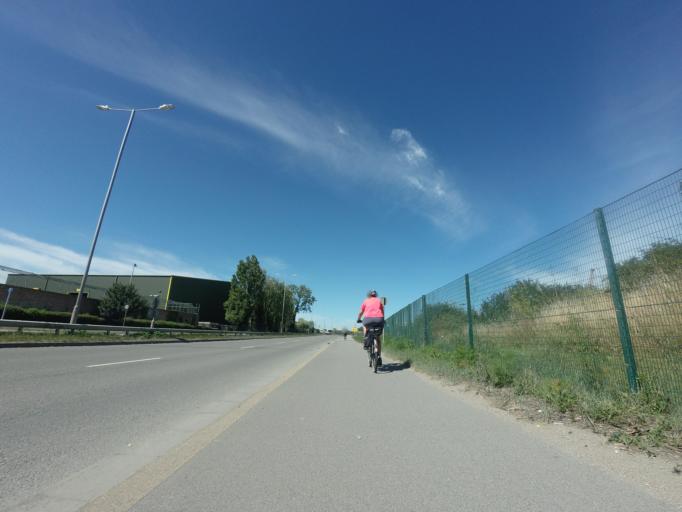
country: GB
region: England
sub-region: Kent
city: Sandwich
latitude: 51.3003
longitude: 1.3471
